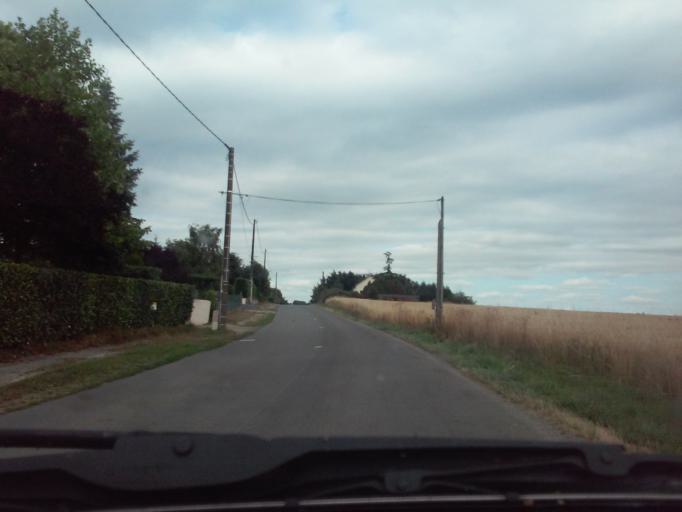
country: FR
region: Brittany
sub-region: Departement d'Ille-et-Vilaine
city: Guichen
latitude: 47.9693
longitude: -1.7594
